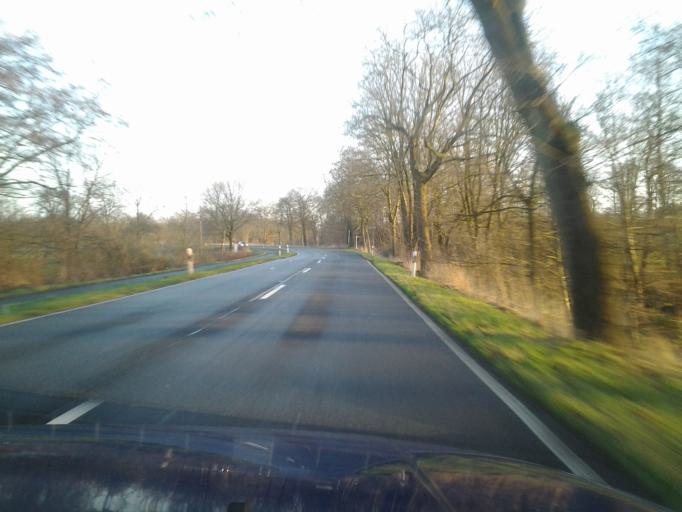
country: DE
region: Lower Saxony
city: Osterholz-Scharmbeck
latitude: 53.1821
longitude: 8.8490
